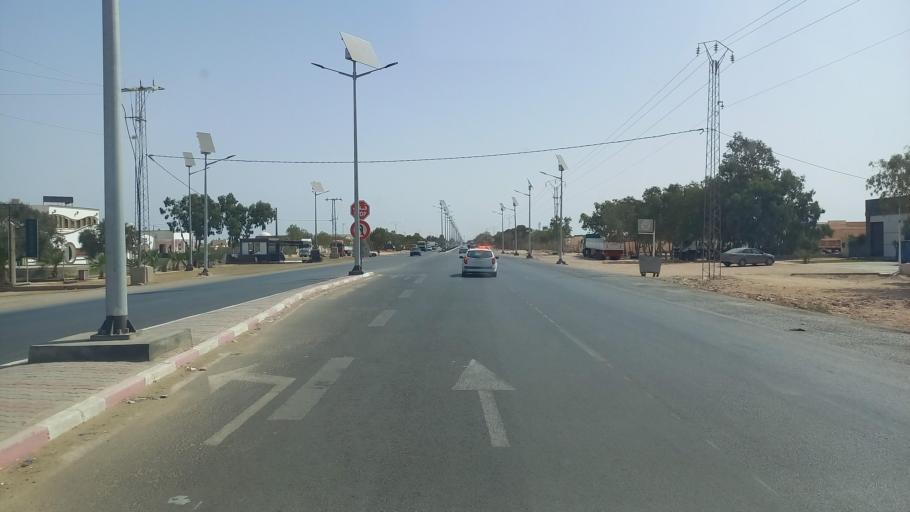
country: TN
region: Madanin
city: Medenine
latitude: 33.3485
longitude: 10.5238
